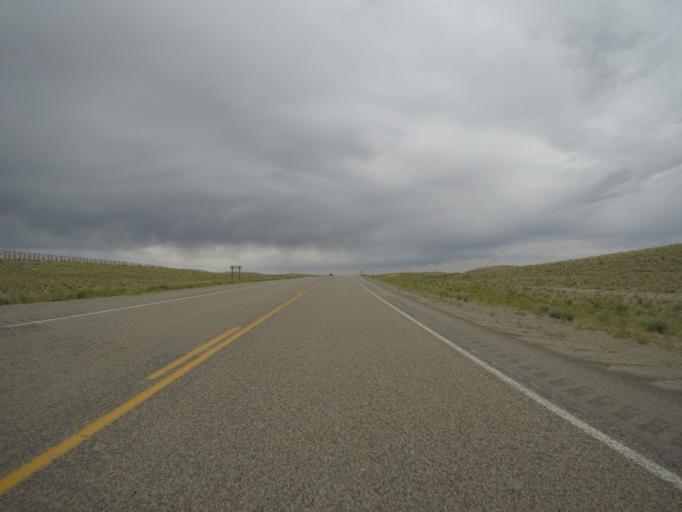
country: US
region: Wyoming
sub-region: Lincoln County
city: Kemmerer
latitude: 41.9759
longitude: -110.0617
